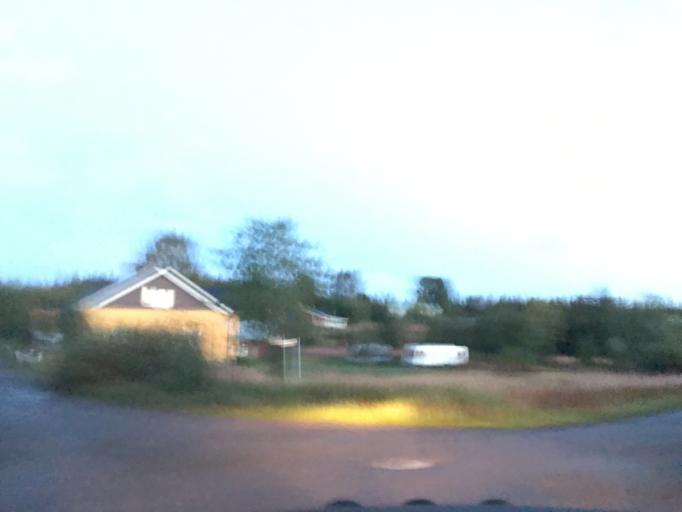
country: SE
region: Norrbotten
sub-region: Gallivare Kommun
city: Malmberget
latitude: 67.6467
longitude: 21.0634
